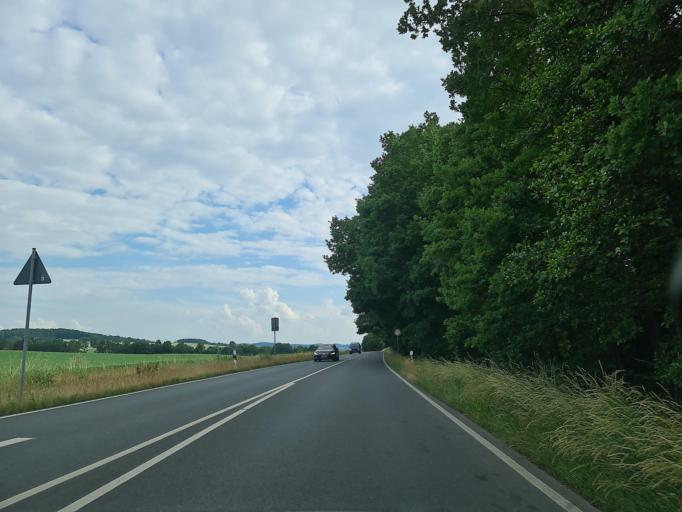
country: DE
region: Saxony
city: Pohl
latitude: 50.5388
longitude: 12.1841
